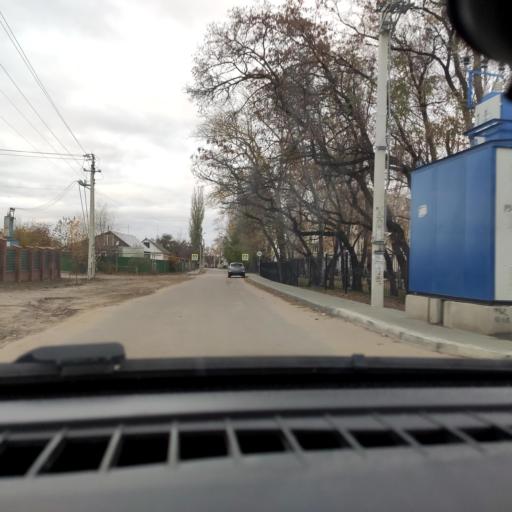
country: RU
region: Voronezj
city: Podgornoye
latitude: 51.7302
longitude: 39.1607
